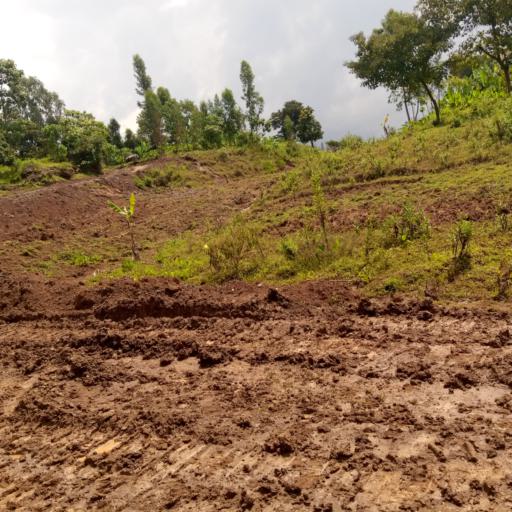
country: ET
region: Southern Nations, Nationalities, and People's Region
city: Arba Minch'
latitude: 6.3164
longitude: 37.3603
